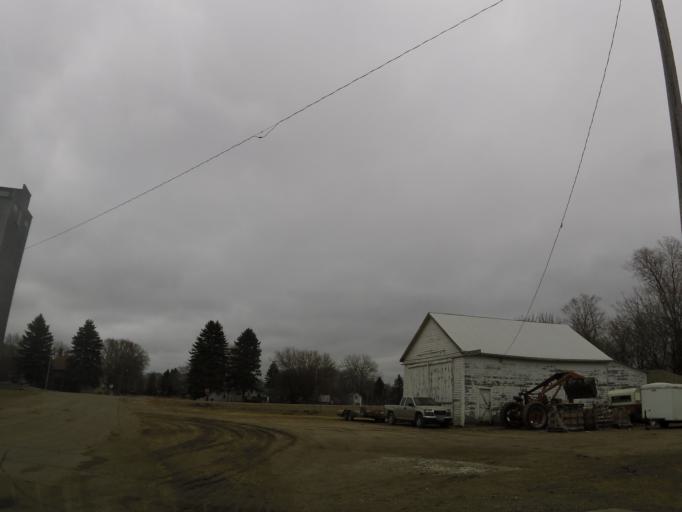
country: US
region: North Dakota
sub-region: Traill County
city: Hillsboro
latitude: 47.1886
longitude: -97.2190
